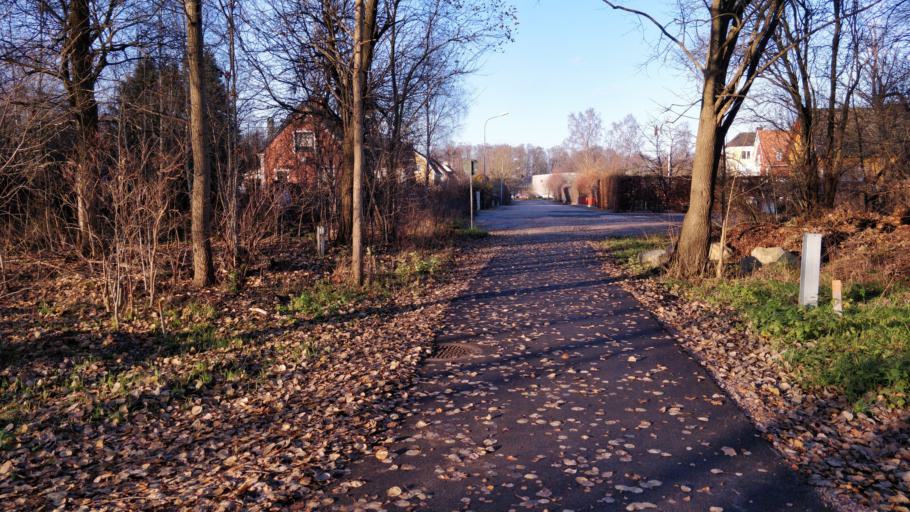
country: SE
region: Kronoberg
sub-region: Almhults Kommun
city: AElmhult
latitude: 56.5461
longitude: 14.1324
